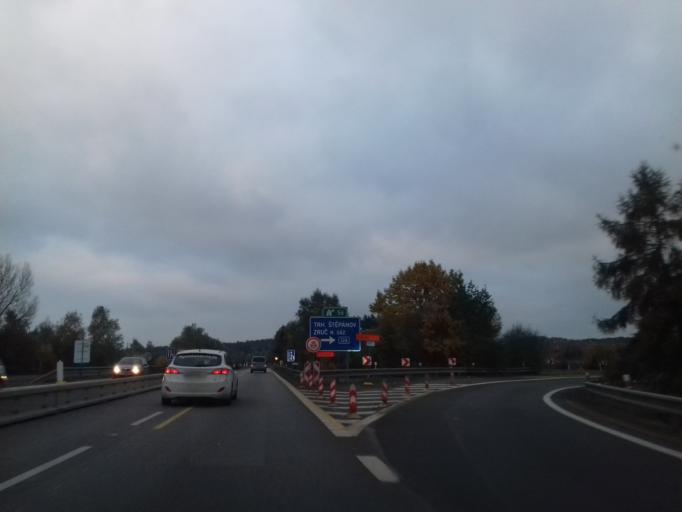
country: CZ
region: Central Bohemia
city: Trhovy Stepanov
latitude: 49.7237
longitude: 15.0486
